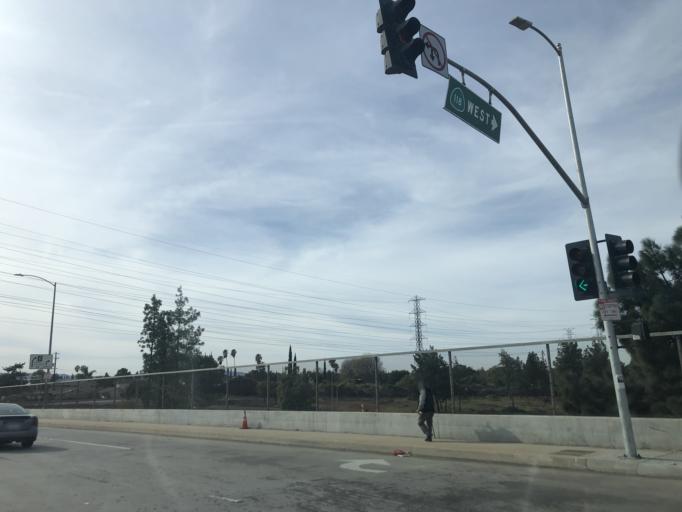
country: US
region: California
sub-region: Los Angeles County
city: Northridge
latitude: 34.2784
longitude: -118.5023
